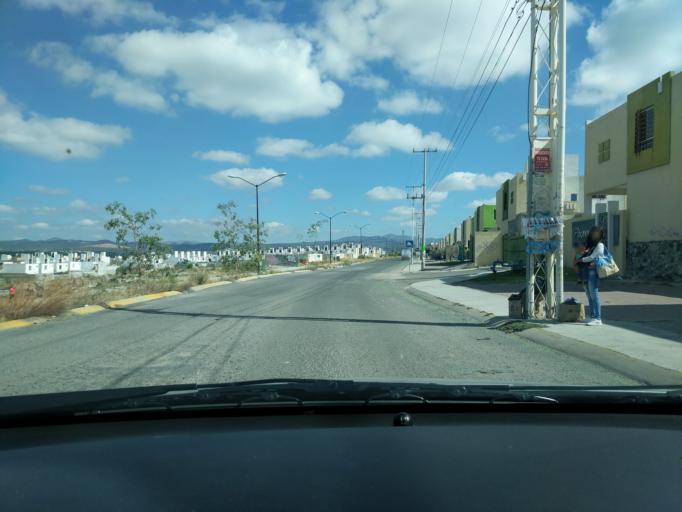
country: MX
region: Queretaro
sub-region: Queretaro
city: Patria Nueva
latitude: 20.6419
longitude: -100.4798
